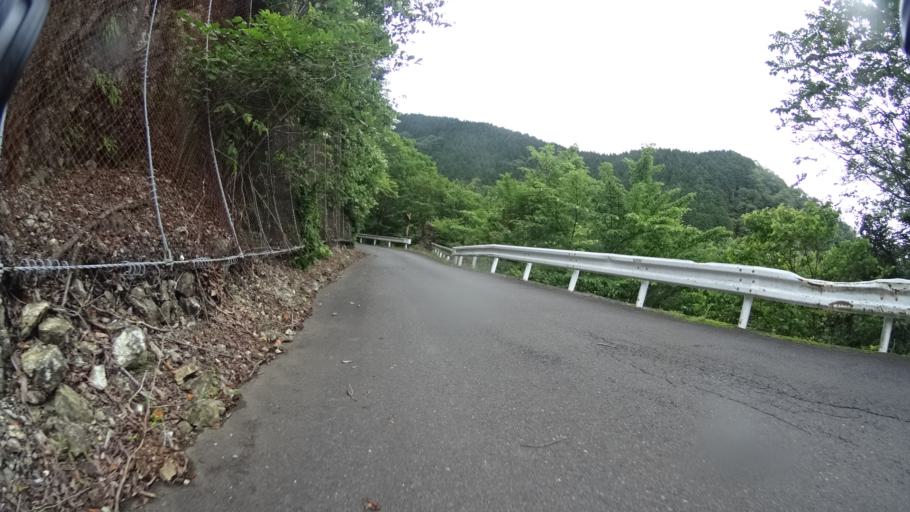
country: JP
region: Saitama
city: Chichibu
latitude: 35.8901
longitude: 139.1221
